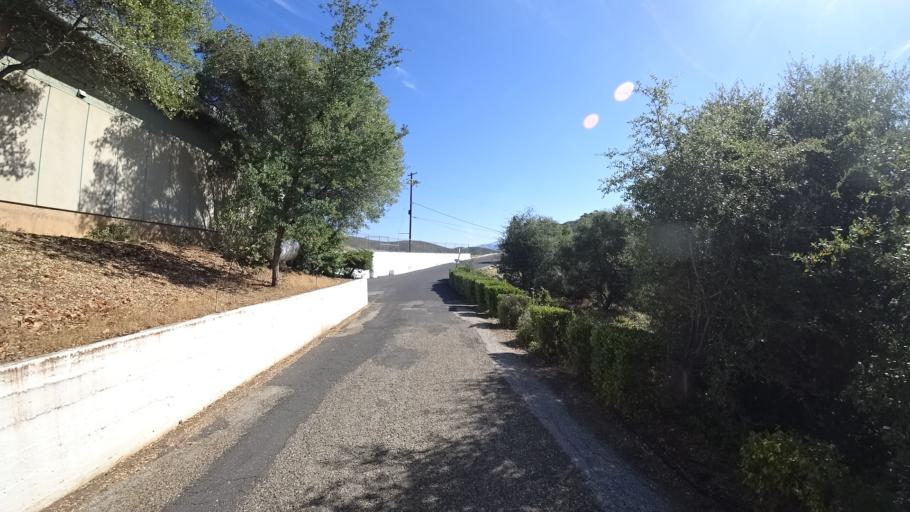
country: US
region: California
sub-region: Calaveras County
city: Mountain Ranch
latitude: 38.1720
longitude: -120.5399
